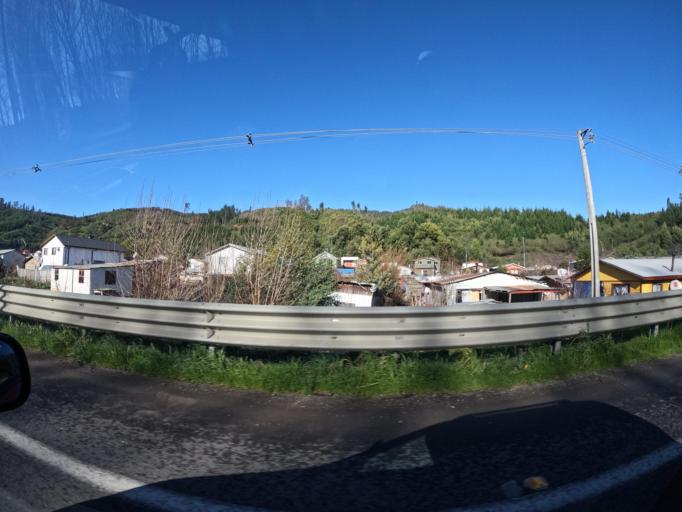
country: CL
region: Biobio
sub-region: Provincia de Concepcion
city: Penco
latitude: -36.8000
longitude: -72.9577
